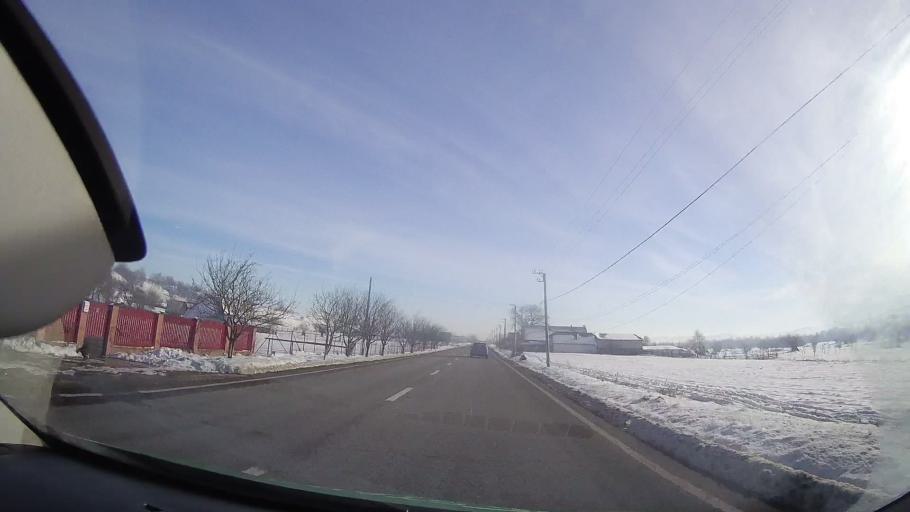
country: RO
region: Neamt
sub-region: Comuna Ghindaoani
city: Ghindaoani
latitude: 47.0863
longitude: 26.3336
